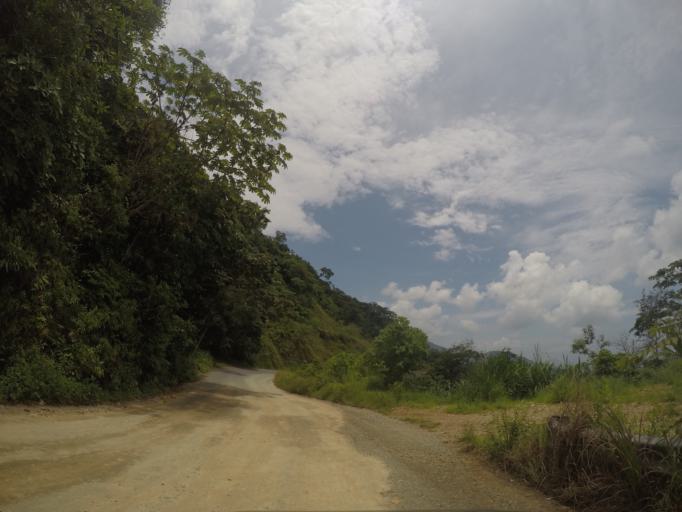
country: MX
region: Oaxaca
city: Pluma Hidalgo
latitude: 15.9086
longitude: -96.4198
